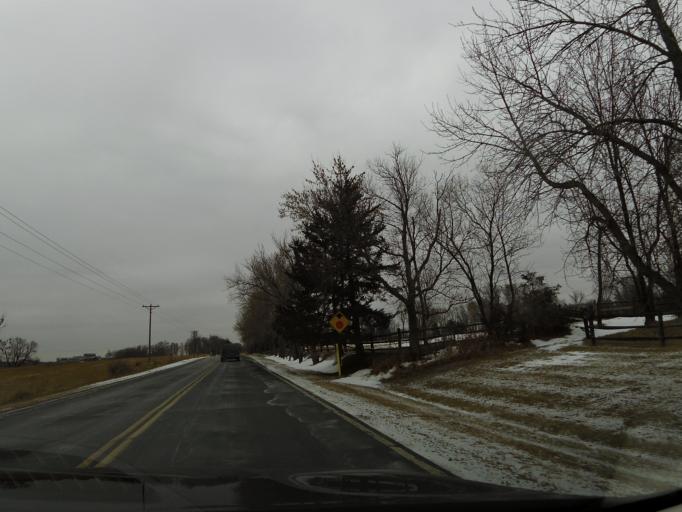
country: US
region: Minnesota
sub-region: Hennepin County
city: Medina
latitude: 45.0345
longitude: -93.5835
